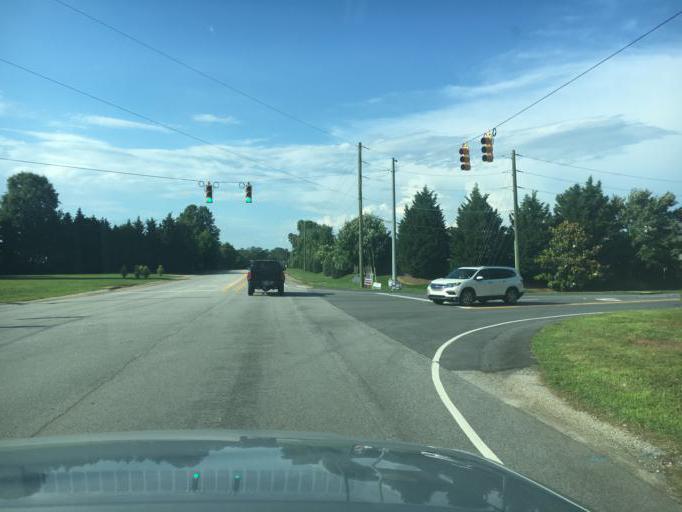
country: US
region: South Carolina
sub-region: Greenville County
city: Simpsonville
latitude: 34.7690
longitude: -82.2581
